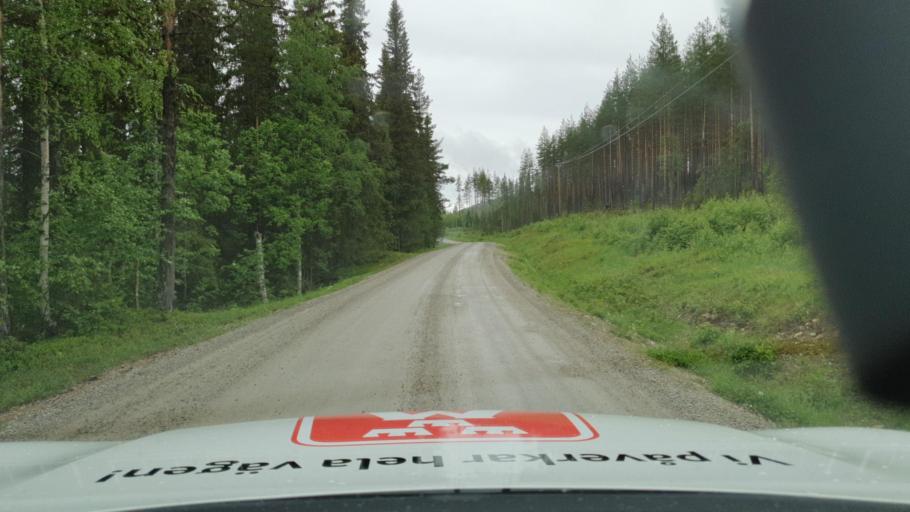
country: SE
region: Vaesterbotten
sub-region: Asele Kommun
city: Asele
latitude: 63.9723
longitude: 17.0518
